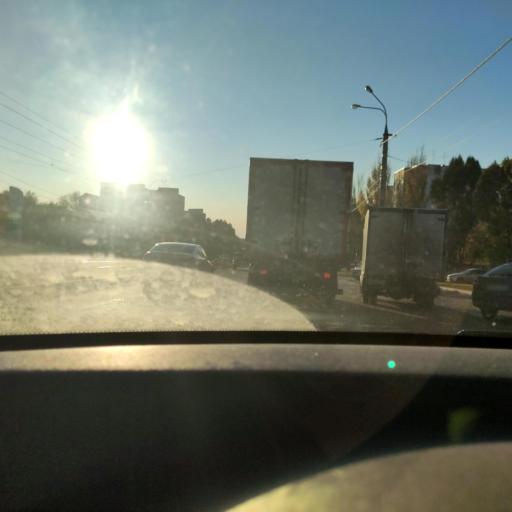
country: RU
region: Samara
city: Samara
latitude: 53.2159
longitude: 50.2232
